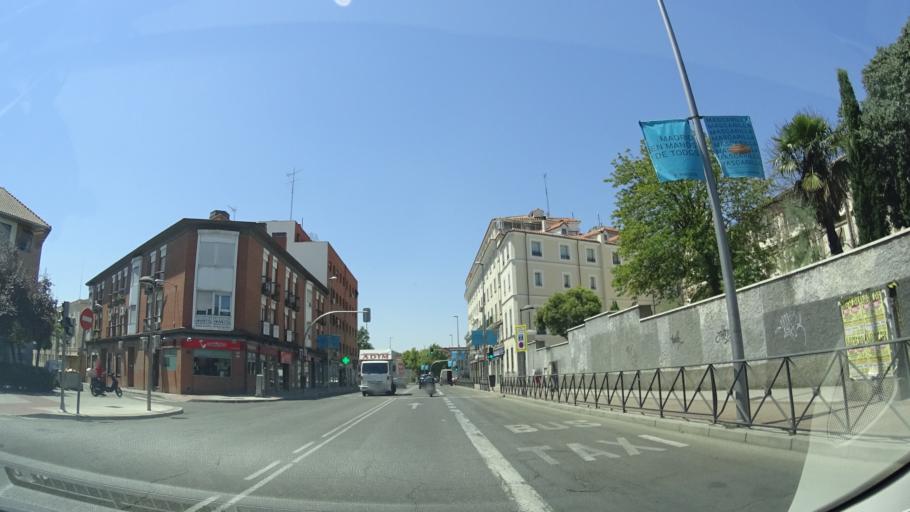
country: ES
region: Madrid
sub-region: Provincia de Madrid
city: Latina
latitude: 40.3839
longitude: -3.7405
